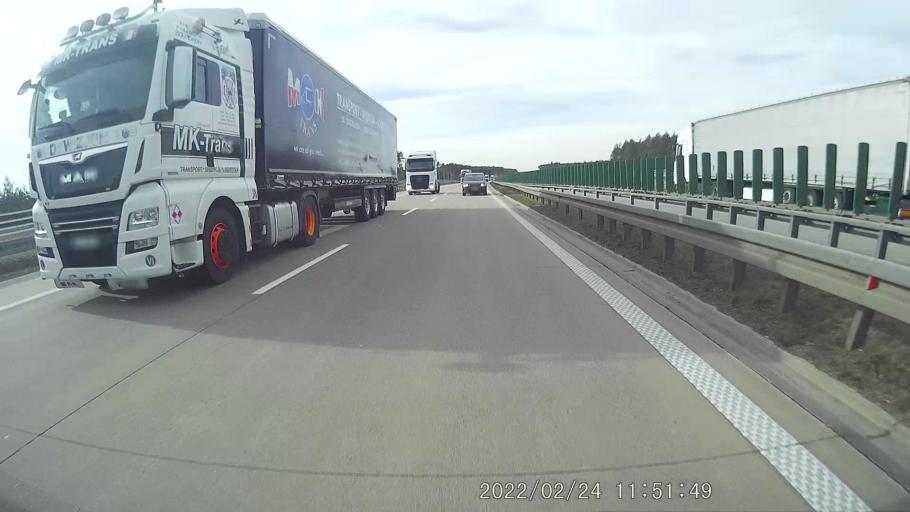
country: PL
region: Lower Silesian Voivodeship
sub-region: Powiat polkowicki
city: Radwanice
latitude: 51.6160
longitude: 15.9716
